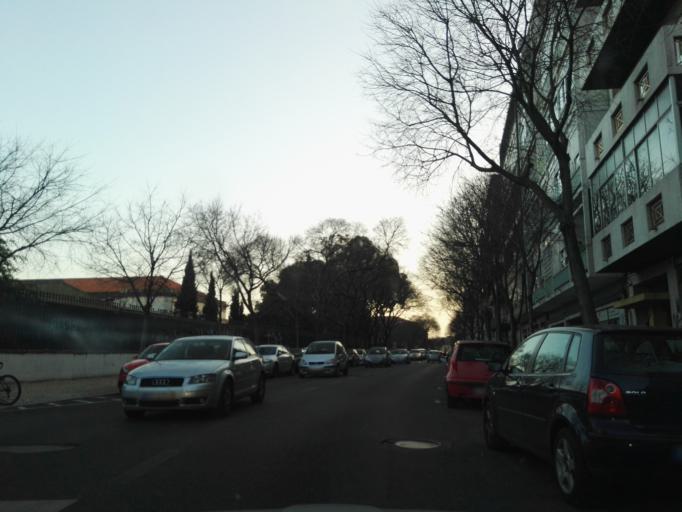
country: PT
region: Lisbon
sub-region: Lisbon
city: Lisbon
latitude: 38.7293
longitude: -9.1404
